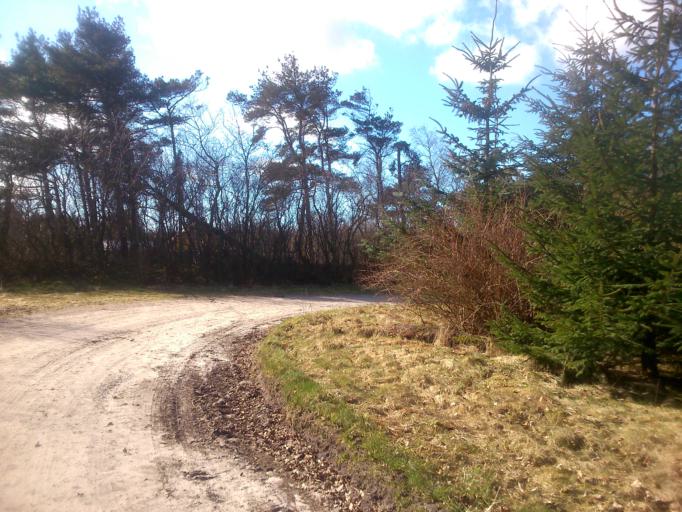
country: DK
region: Central Jutland
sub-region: Ringkobing-Skjern Kommune
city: Skjern
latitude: 55.9644
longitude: 8.4506
